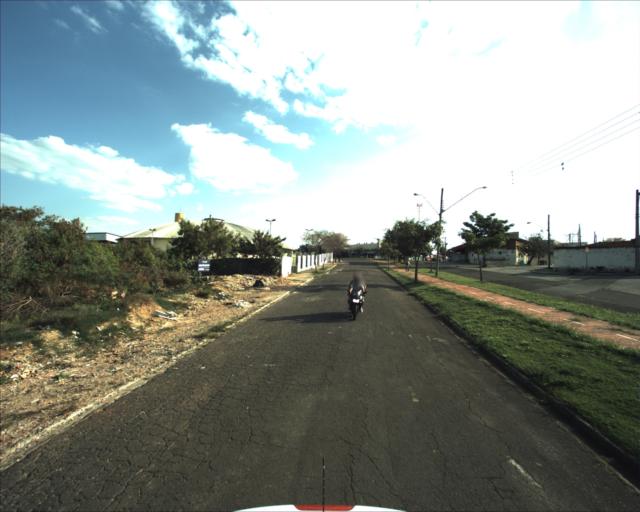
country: BR
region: Sao Paulo
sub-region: Sorocaba
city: Sorocaba
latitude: -23.5024
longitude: -47.5147
